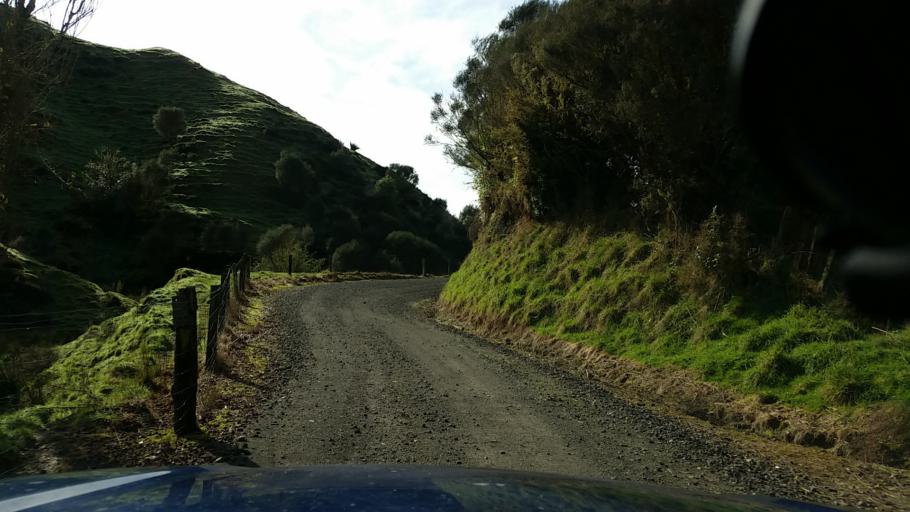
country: NZ
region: Taranaki
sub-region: New Plymouth District
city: Waitara
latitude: -39.0335
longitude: 174.7751
